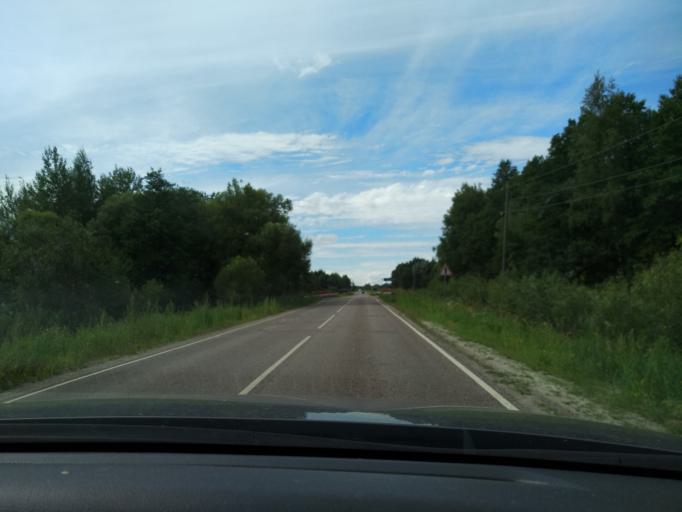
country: RU
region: Moskovskaya
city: Krasnyy Tkach
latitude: 55.3888
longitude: 39.1737
